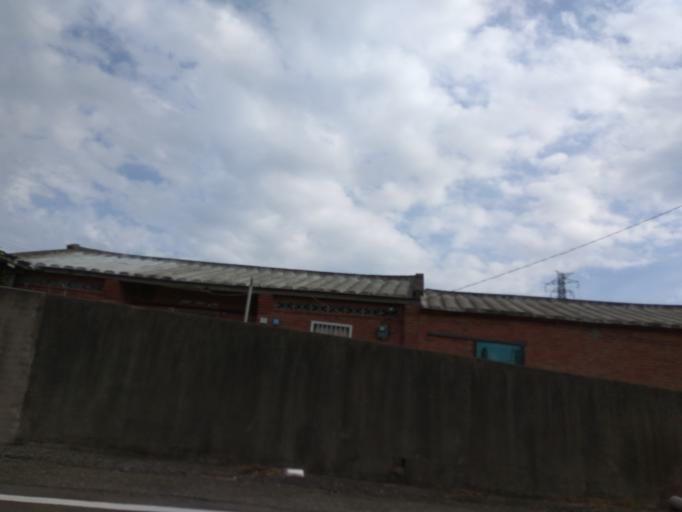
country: TW
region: Taiwan
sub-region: Hsinchu
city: Zhubei
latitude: 24.9727
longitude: 121.0184
